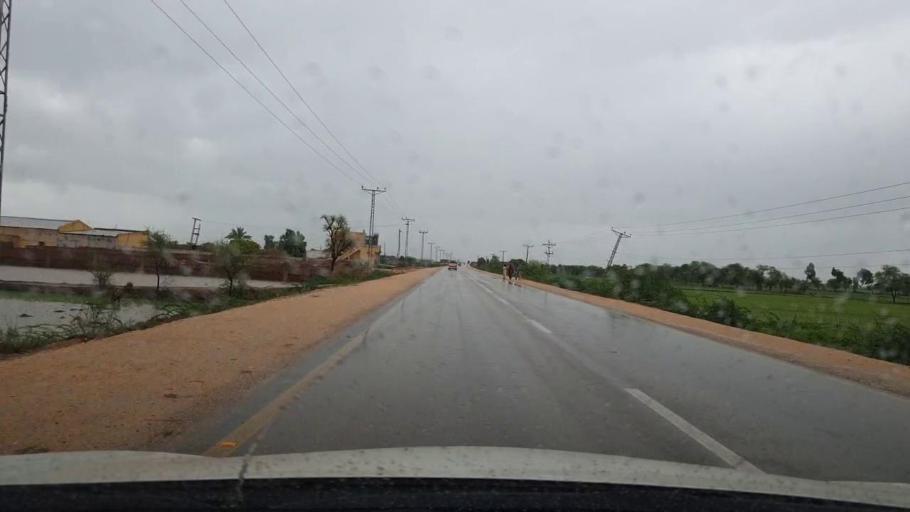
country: PK
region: Sindh
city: Kario
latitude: 24.6536
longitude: 68.5459
